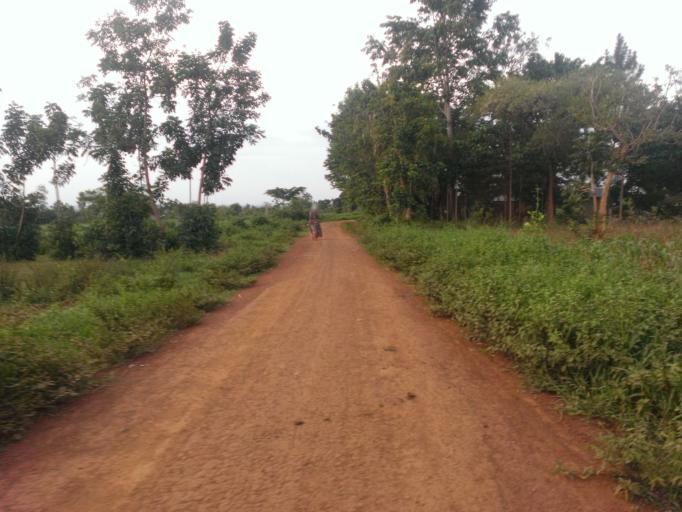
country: UG
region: Eastern Region
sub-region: Busia District
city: Busia
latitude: 0.5361
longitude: 34.0424
